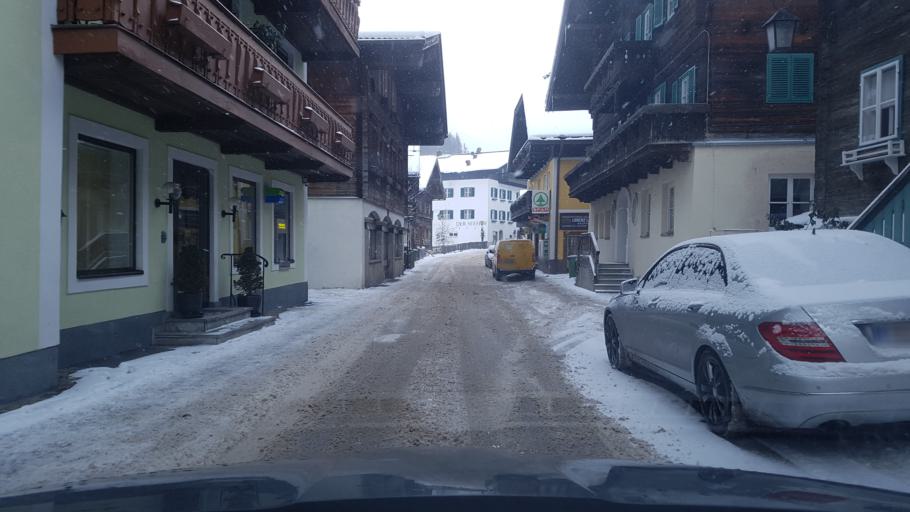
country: AT
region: Salzburg
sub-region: Politischer Bezirk Sankt Johann im Pongau
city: Goldegg
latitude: 47.3184
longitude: 13.0993
